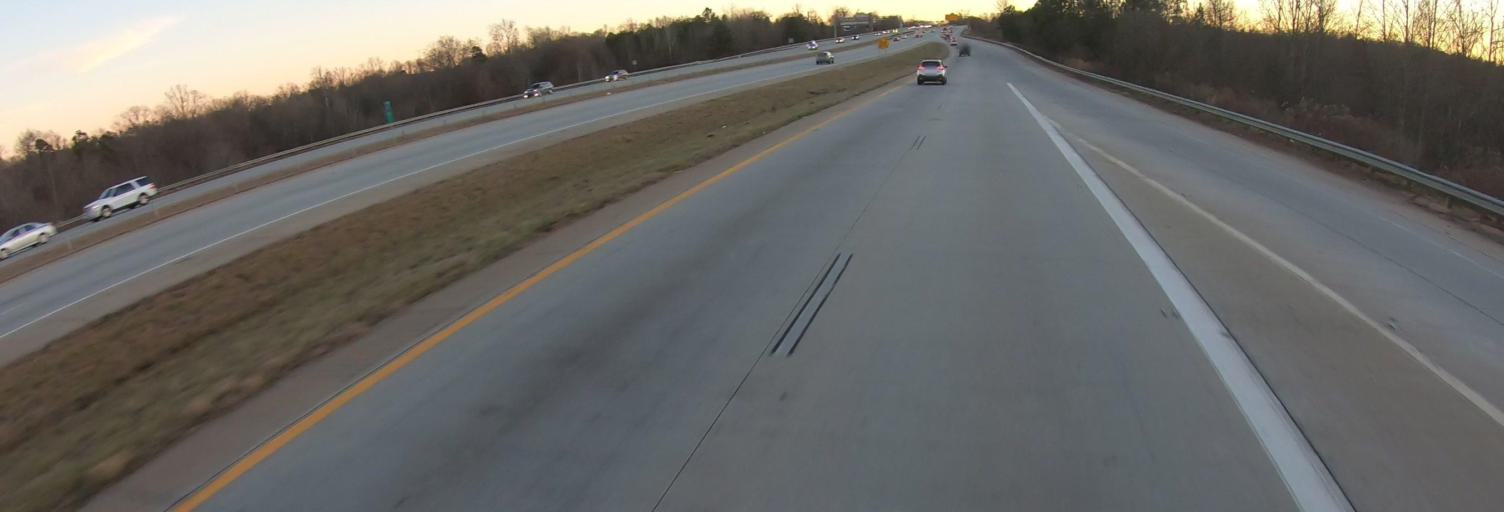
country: US
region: North Carolina
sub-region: Gaston County
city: Belmont
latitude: 35.2366
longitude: -80.9711
